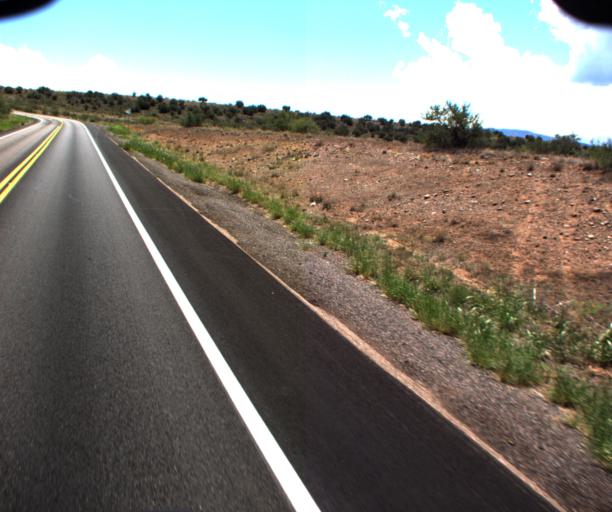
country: US
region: Arizona
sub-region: Yavapai County
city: Camp Verde
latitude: 34.5122
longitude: -111.7732
